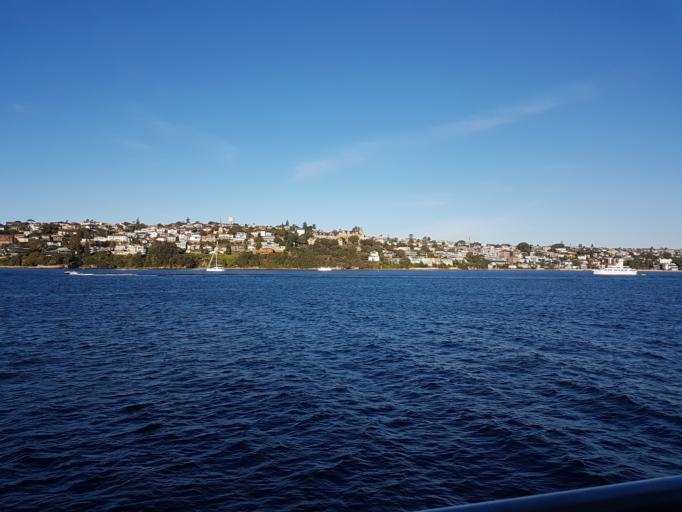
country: AU
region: New South Wales
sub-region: Woollahra
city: Point Piper
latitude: -33.8608
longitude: 151.2609
